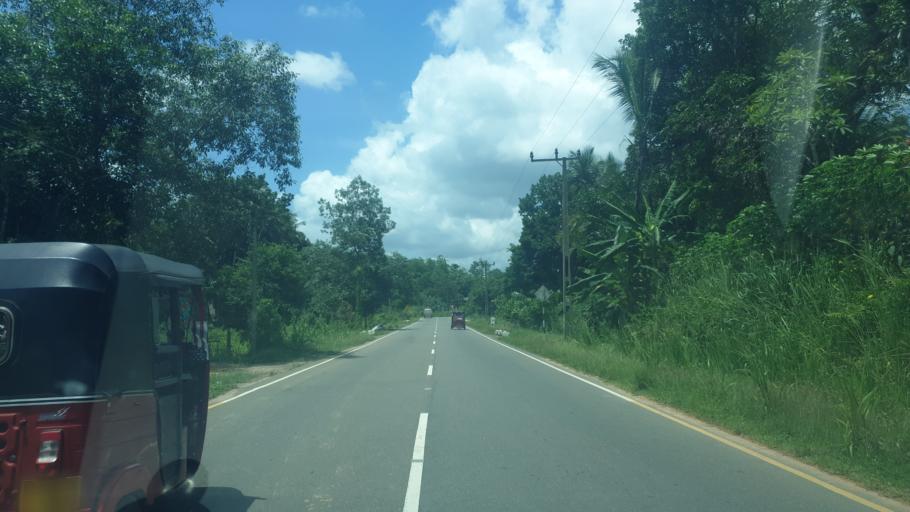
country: LK
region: Western
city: Horawala Junction
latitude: 6.5150
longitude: 80.2392
